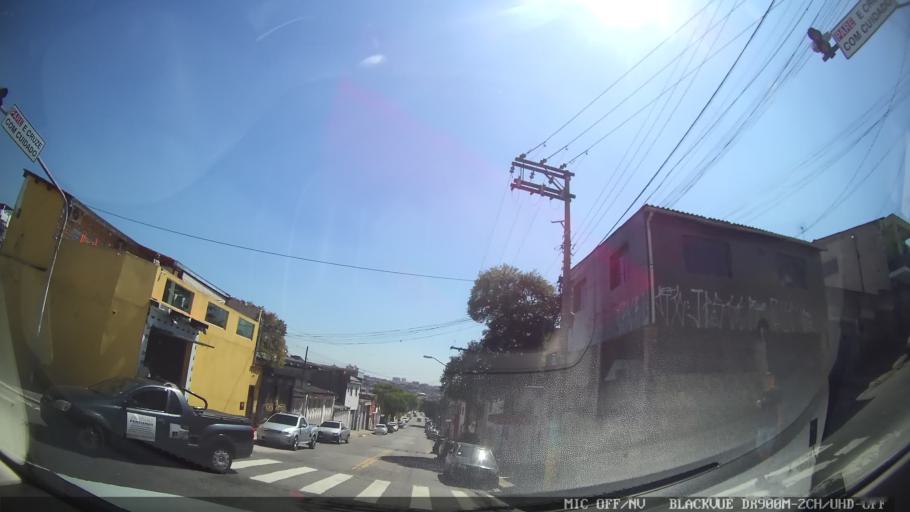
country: BR
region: Sao Paulo
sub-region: Sao Paulo
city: Sao Paulo
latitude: -23.5001
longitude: -46.6571
